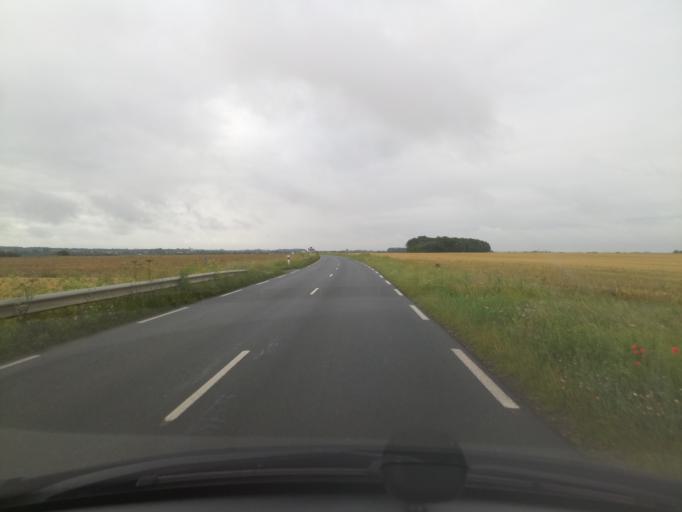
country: FR
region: Poitou-Charentes
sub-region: Departement de la Charente-Maritime
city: Saint-Jean-de-Liversay
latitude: 46.2023
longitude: -0.8726
